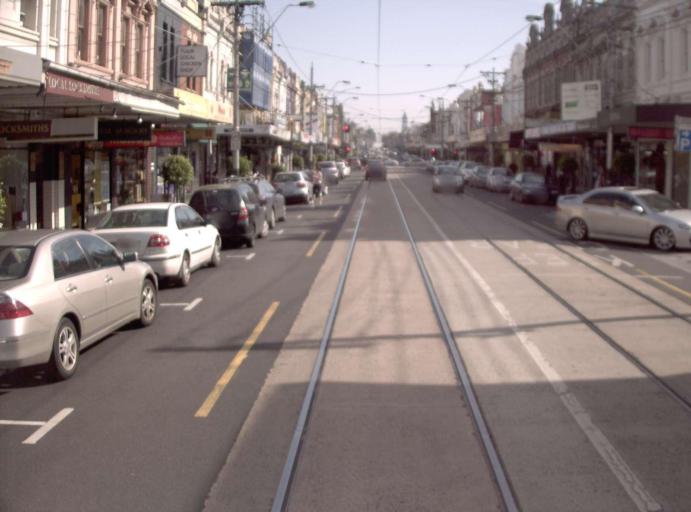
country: AU
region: Victoria
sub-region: Glen Eira
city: Caulfield North
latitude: -37.8637
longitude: 145.0281
